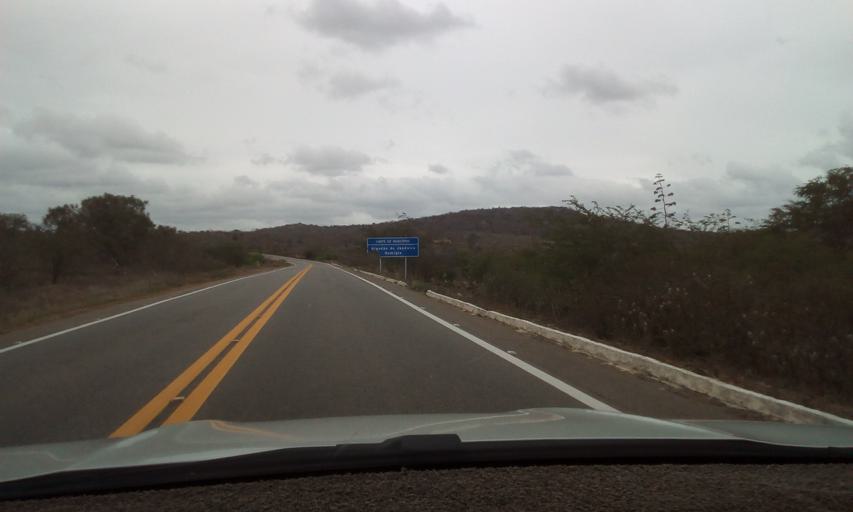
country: BR
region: Paraiba
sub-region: Areia
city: Remigio
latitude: -6.8909
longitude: -35.9024
